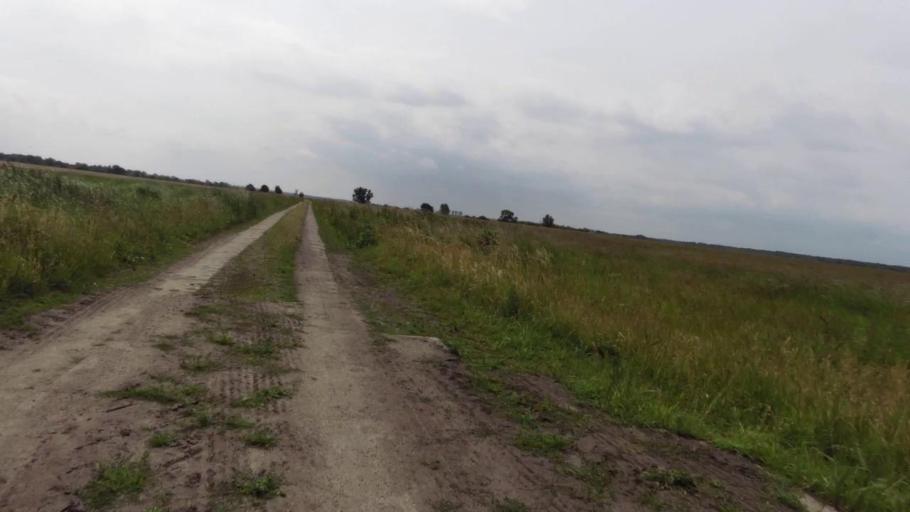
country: PL
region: West Pomeranian Voivodeship
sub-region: Powiat kamienski
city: Wolin
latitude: 53.7502
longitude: 14.6223
